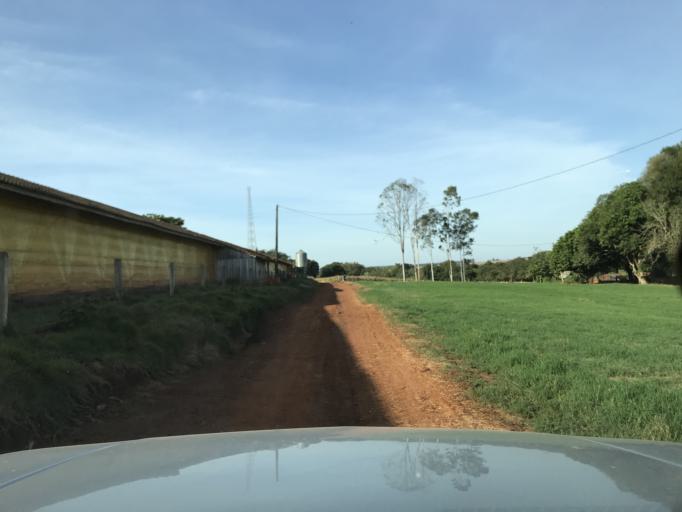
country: BR
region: Parana
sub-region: Palotina
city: Palotina
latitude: -24.2481
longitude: -53.7468
